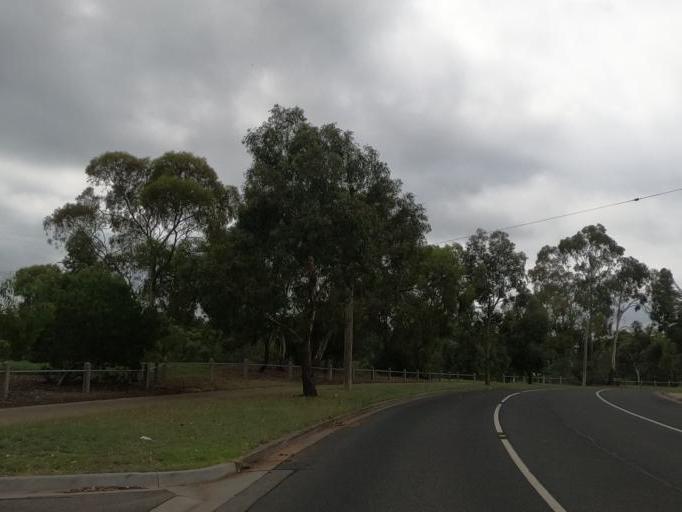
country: AU
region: Victoria
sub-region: Hume
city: Jacana
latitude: -37.6800
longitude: 144.9049
